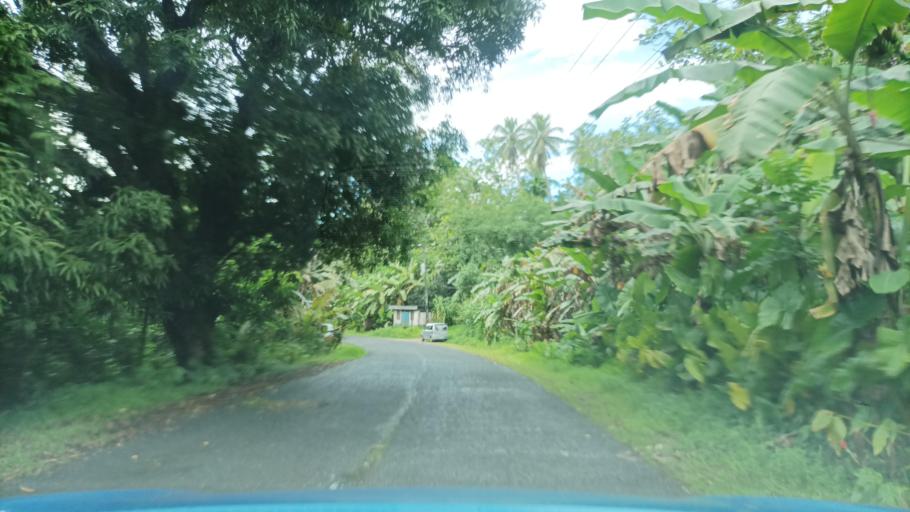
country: FM
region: Pohnpei
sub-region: Sokehs Municipality
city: Palikir - National Government Center
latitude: 6.8223
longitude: 158.1575
